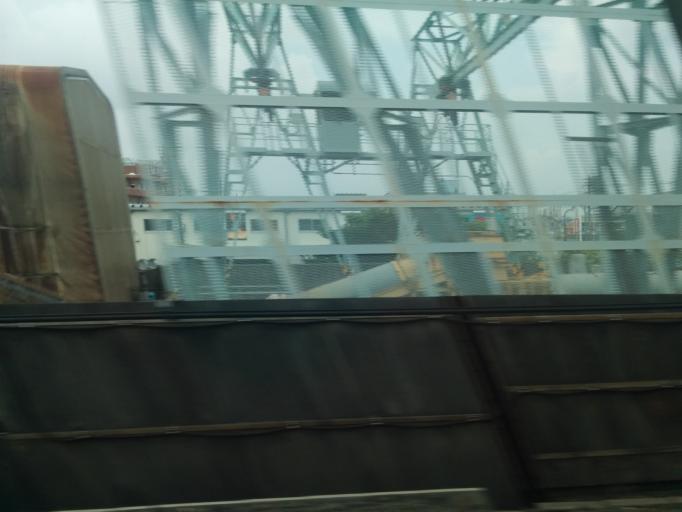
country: JP
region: Aichi
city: Toyohashi
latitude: 34.7690
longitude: 137.3780
